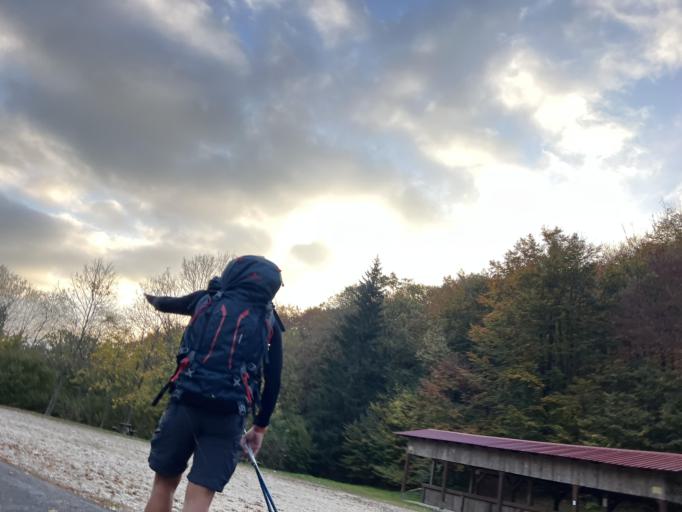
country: IT
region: Friuli Venezia Giulia
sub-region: Provincia di Pordenone
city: Andreis
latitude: 46.1958
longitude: 12.6587
